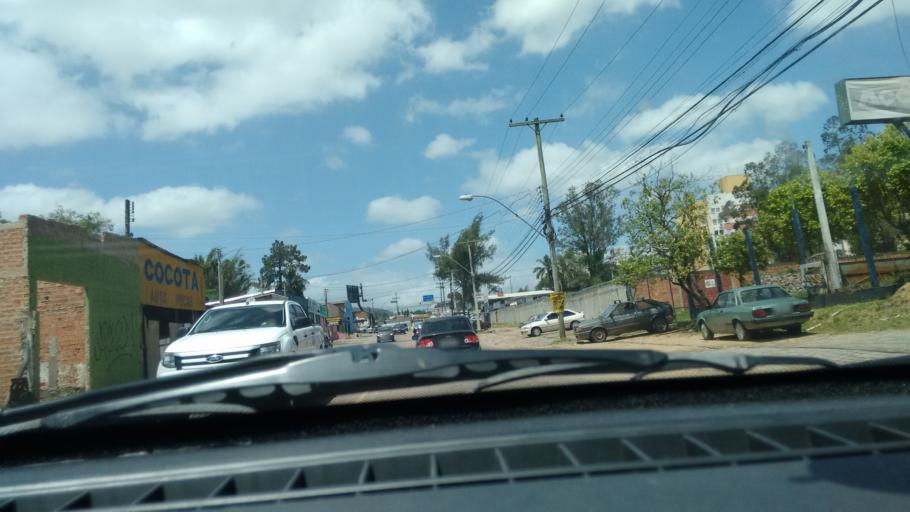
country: BR
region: Rio Grande do Sul
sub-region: Cachoeirinha
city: Cachoeirinha
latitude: -30.0098
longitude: -51.1283
